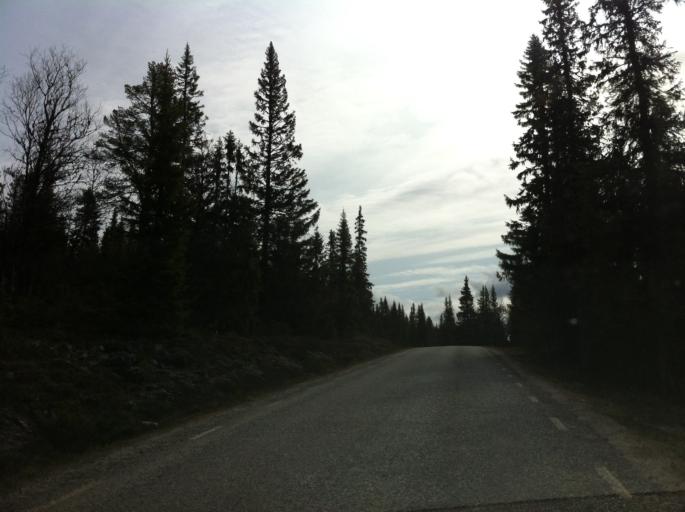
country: NO
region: Hedmark
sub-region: Engerdal
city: Engerdal
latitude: 62.3053
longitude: 12.8028
